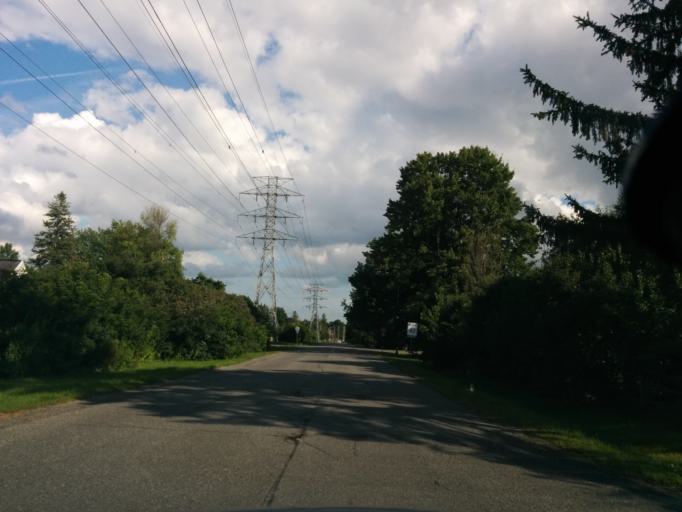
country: CA
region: Ontario
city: Ottawa
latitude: 45.3551
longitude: -75.7448
